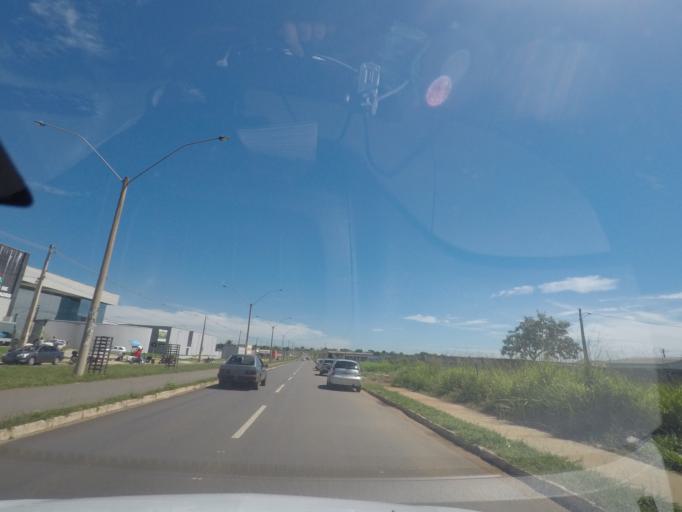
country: BR
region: Goias
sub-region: Aparecida De Goiania
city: Aparecida de Goiania
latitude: -16.7994
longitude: -49.3287
